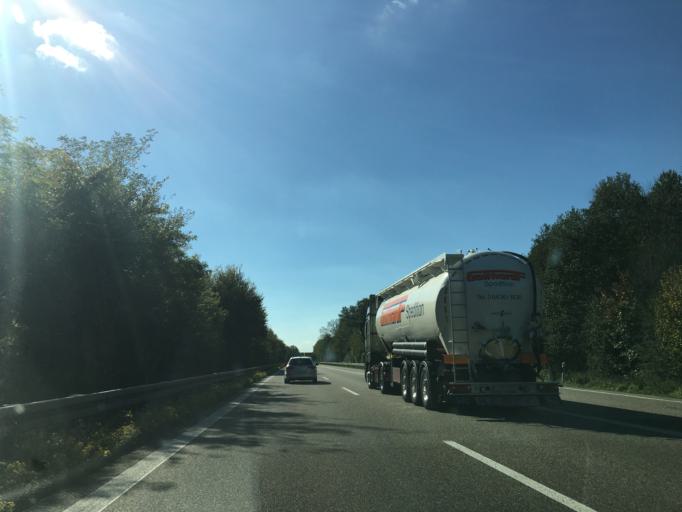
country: DE
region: Baden-Wuerttemberg
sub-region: Freiburg Region
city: Schallstadt
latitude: 47.9898
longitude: 7.7460
